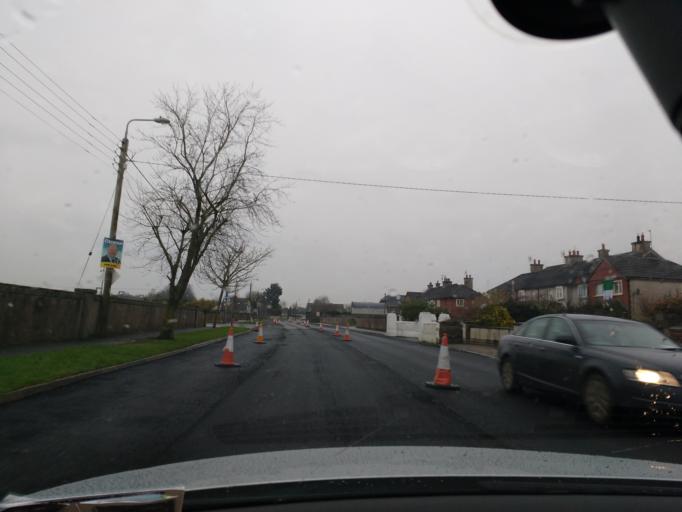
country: IE
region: Munster
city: Thurles
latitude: 52.6701
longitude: -7.8215
